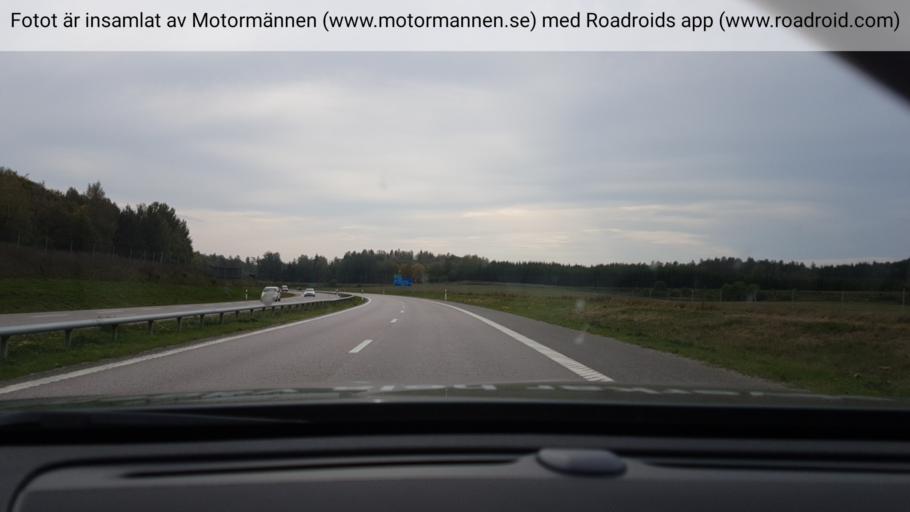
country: SE
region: Stockholm
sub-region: Nynashamns Kommun
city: Osmo
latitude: 58.9538
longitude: 17.9022
